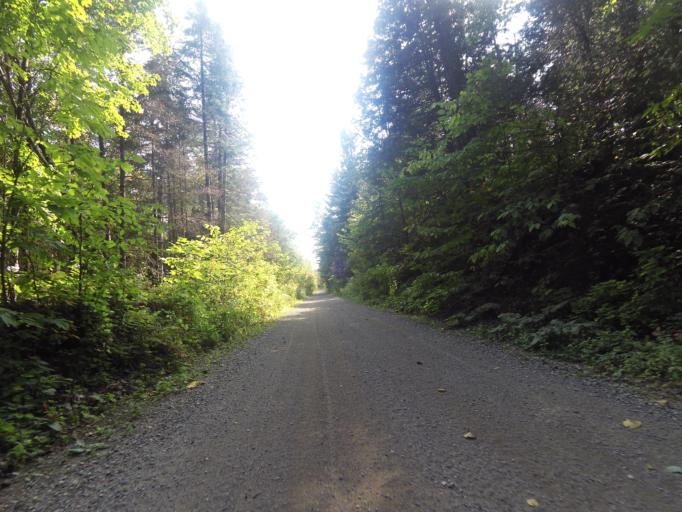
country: CA
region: Ontario
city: Renfrew
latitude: 45.1517
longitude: -76.6879
